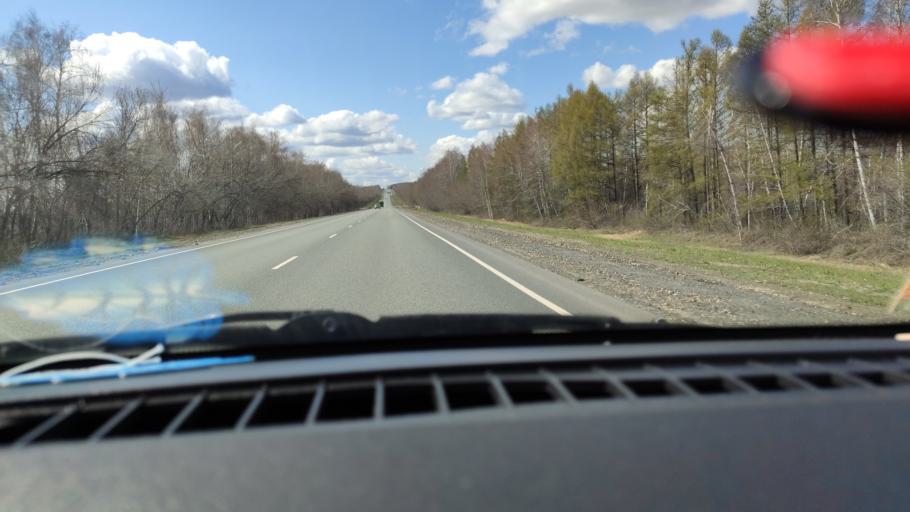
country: RU
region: Saratov
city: Khvalynsk
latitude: 52.5726
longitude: 48.1049
